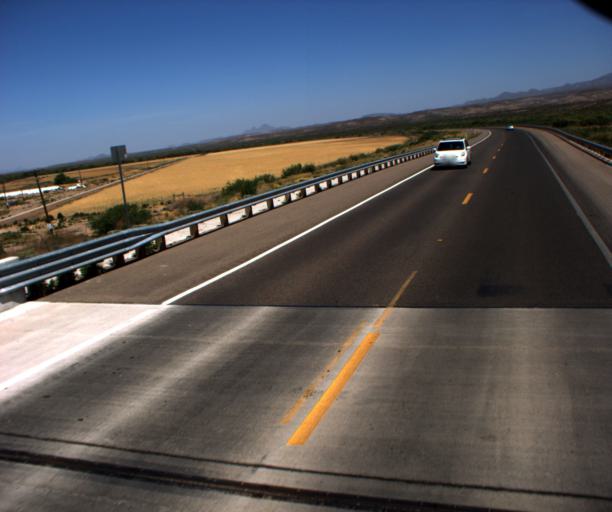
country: US
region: Arizona
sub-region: Graham County
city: Bylas
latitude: 33.1673
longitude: -110.1352
